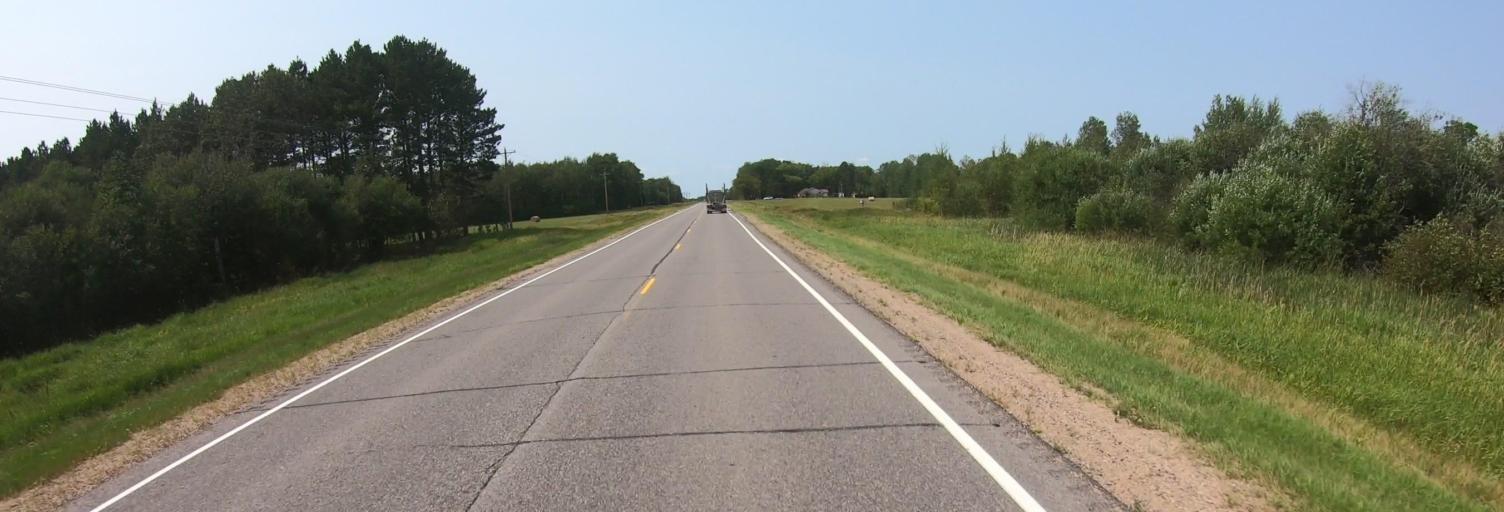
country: US
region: Minnesota
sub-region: Koochiching County
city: International Falls
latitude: 48.5182
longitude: -93.6170
